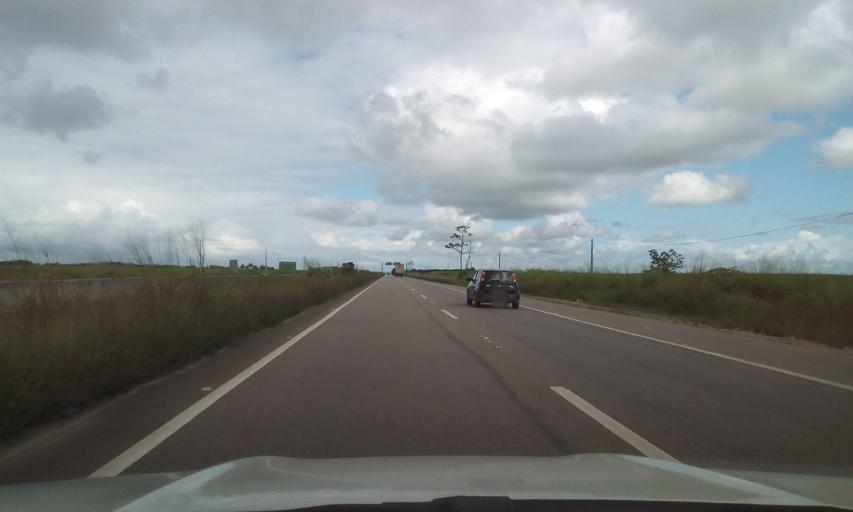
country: BR
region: Pernambuco
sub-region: Itapissuma
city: Itapissuma
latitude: -7.6688
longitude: -34.9329
